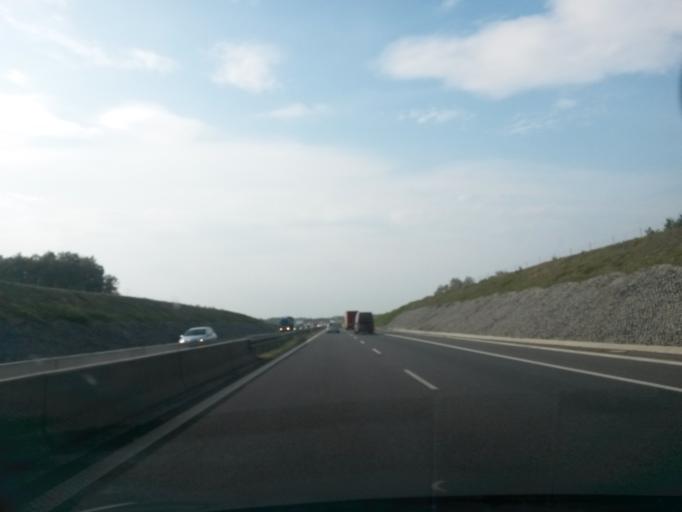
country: PL
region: Lesser Poland Voivodeship
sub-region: Powiat bochenski
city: Jodlowka
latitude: 50.0005
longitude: 20.5521
